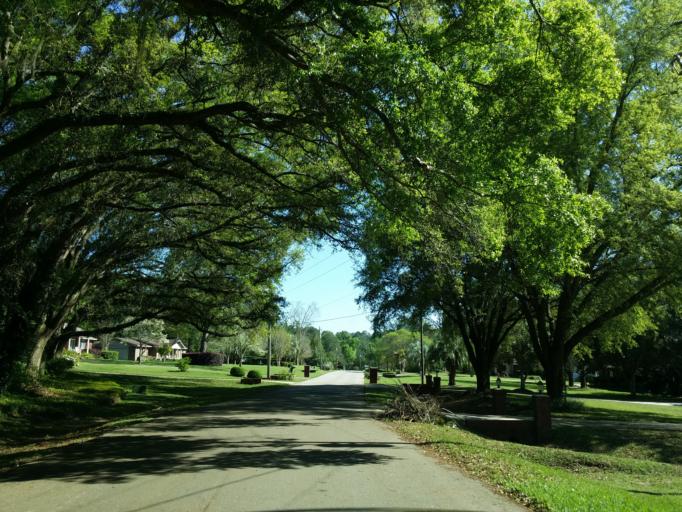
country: US
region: Florida
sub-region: Leon County
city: Tallahassee
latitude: 30.4842
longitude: -84.1821
